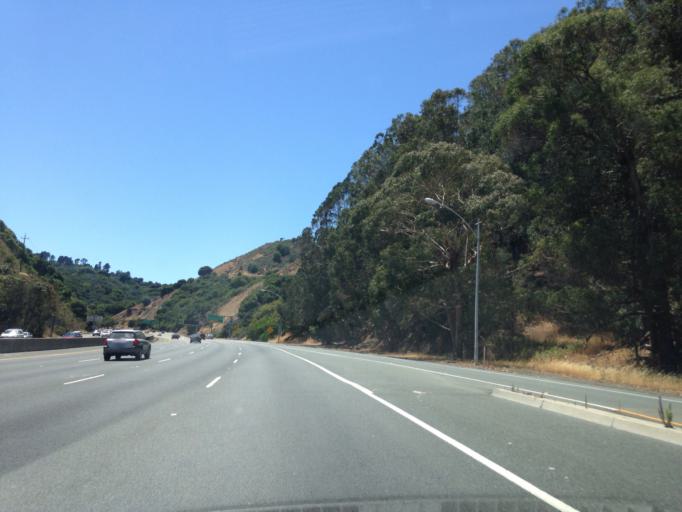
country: US
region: California
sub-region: Contra Costa County
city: Orinda
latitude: 37.8674
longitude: -122.2019
